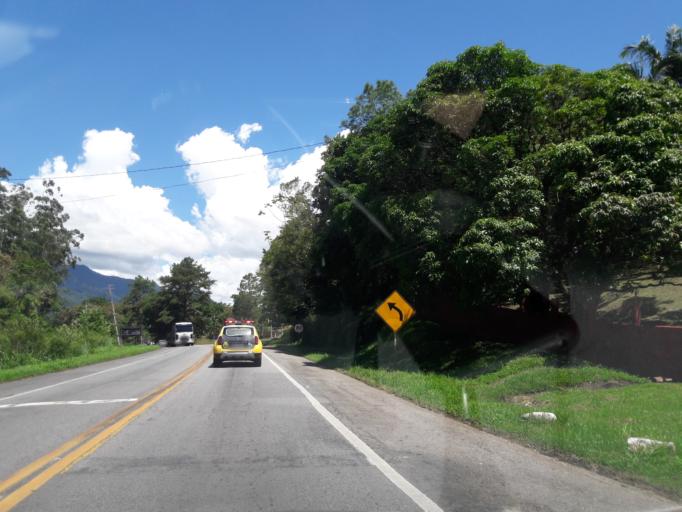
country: BR
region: Parana
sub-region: Antonina
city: Antonina
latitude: -25.5249
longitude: -48.7960
